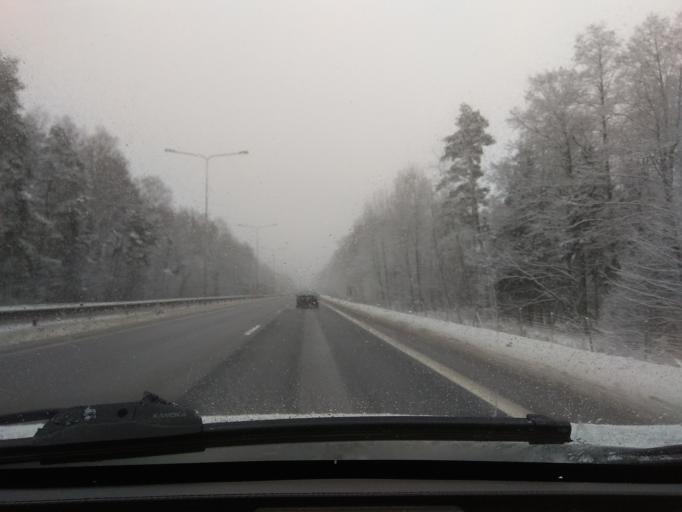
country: LT
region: Kauno apskritis
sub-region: Kauno rajonas
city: Karmelava
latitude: 54.9053
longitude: 24.1215
